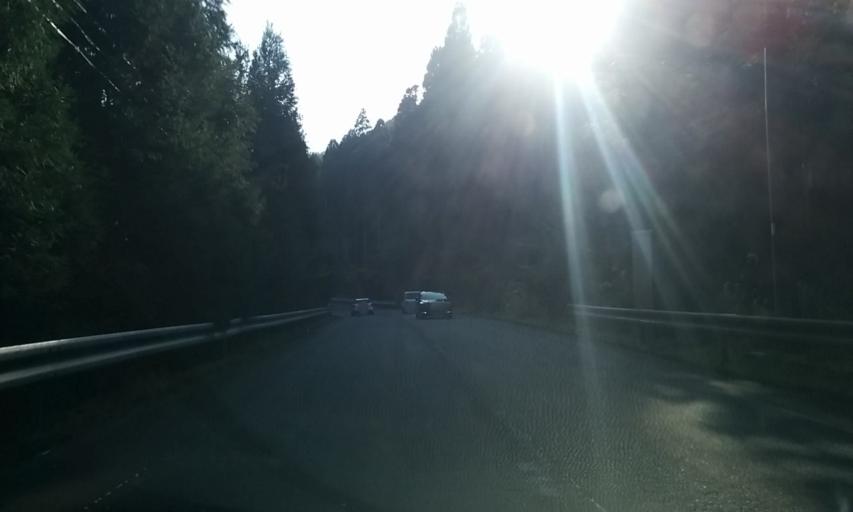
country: JP
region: Kyoto
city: Kameoka
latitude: 35.2200
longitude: 135.5708
